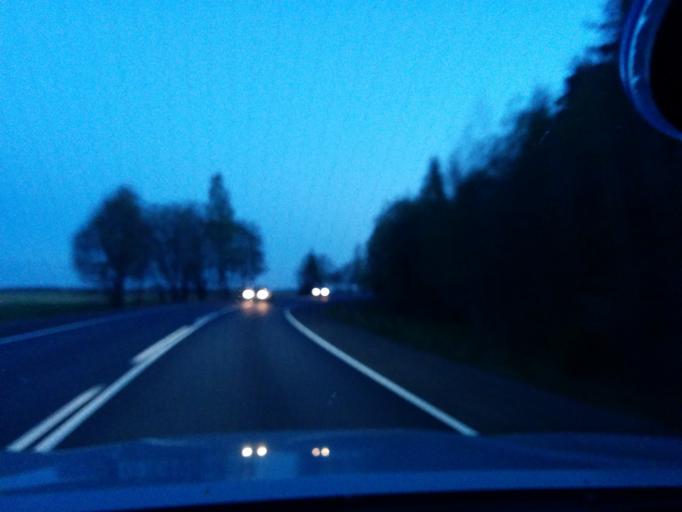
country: RU
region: Leningrad
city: Verkhniye Osel'ki
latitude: 60.1890
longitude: 30.4115
